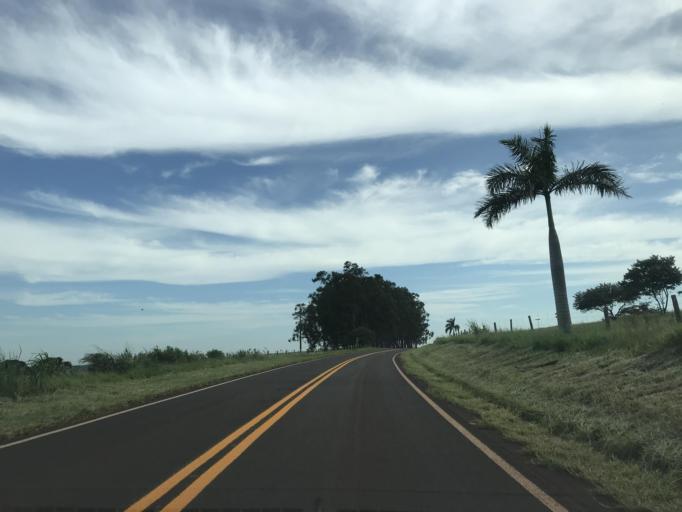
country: BR
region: Parana
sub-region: Terra Rica
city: Terra Rica
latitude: -22.7812
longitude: -52.6573
